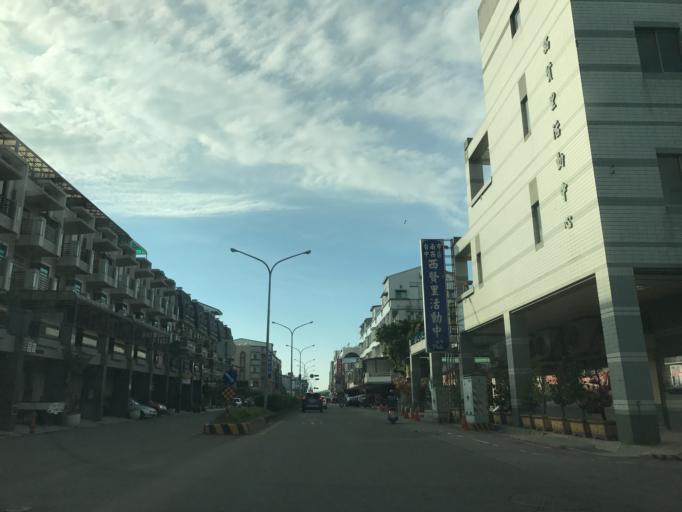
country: TW
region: Taiwan
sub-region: Tainan
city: Tainan
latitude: 22.9996
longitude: 120.1740
